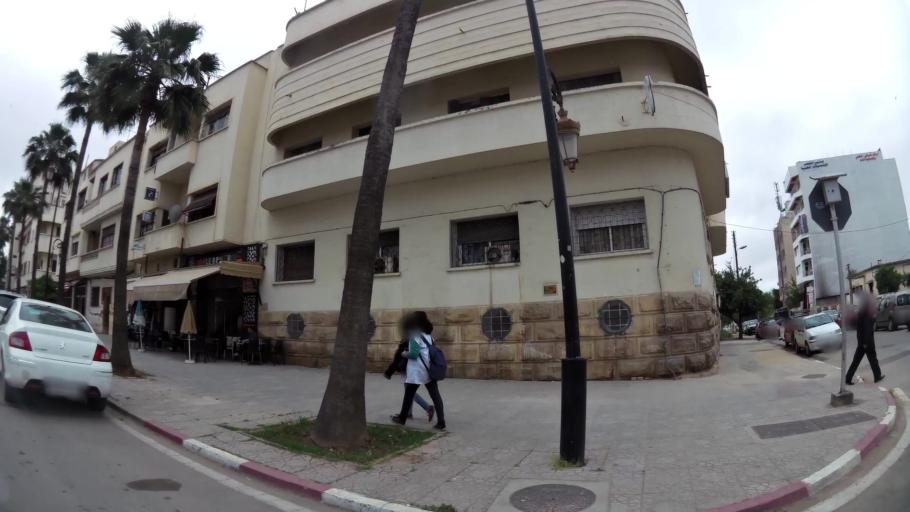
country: MA
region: Fes-Boulemane
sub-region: Fes
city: Fes
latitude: 34.0461
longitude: -4.9967
